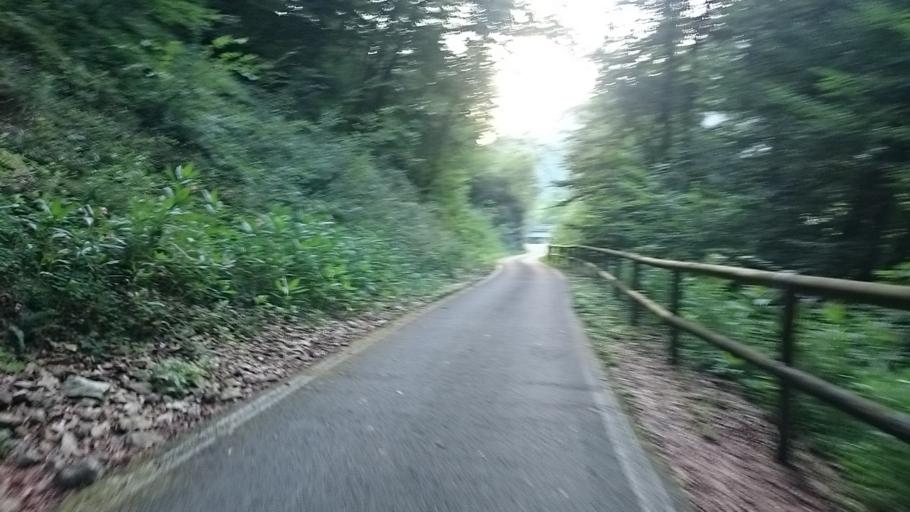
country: IT
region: Veneto
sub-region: Provincia di Vicenza
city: Enego
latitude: 45.9522
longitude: 11.7220
